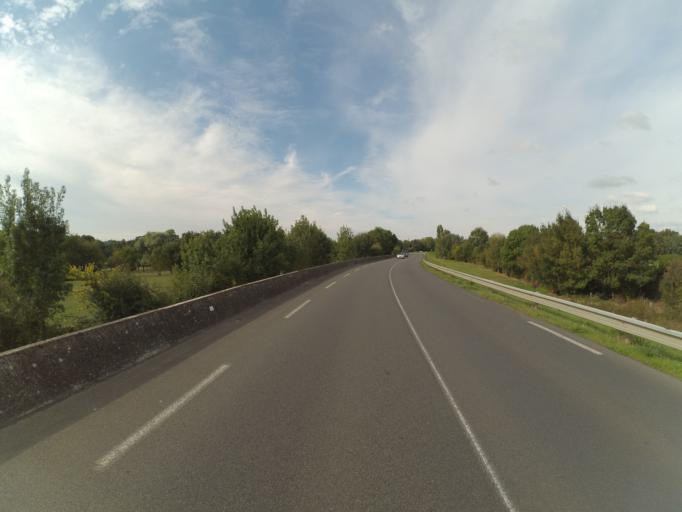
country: FR
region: Pays de la Loire
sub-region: Departement de Maine-et-Loire
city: Villebernier
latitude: 47.2571
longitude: -0.0426
